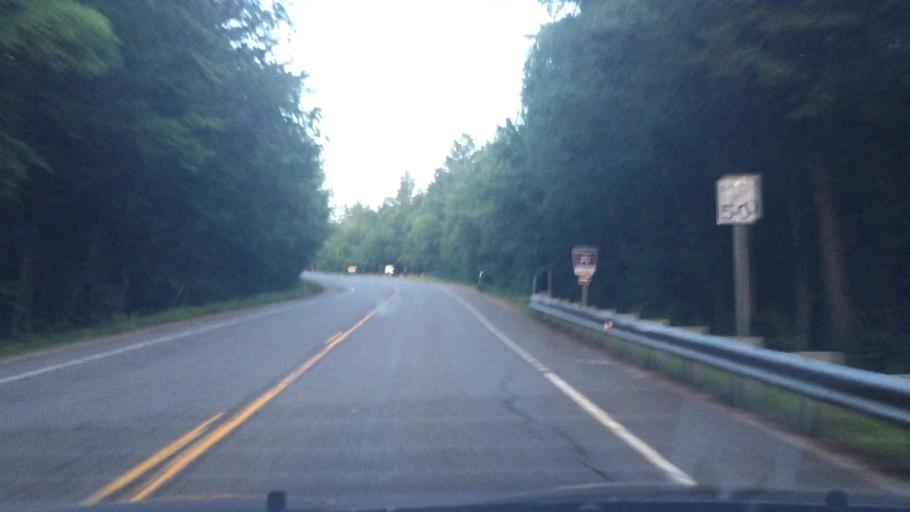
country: US
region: New Hampshire
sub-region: Grafton County
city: Woodstock
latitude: 44.0402
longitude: -71.5445
